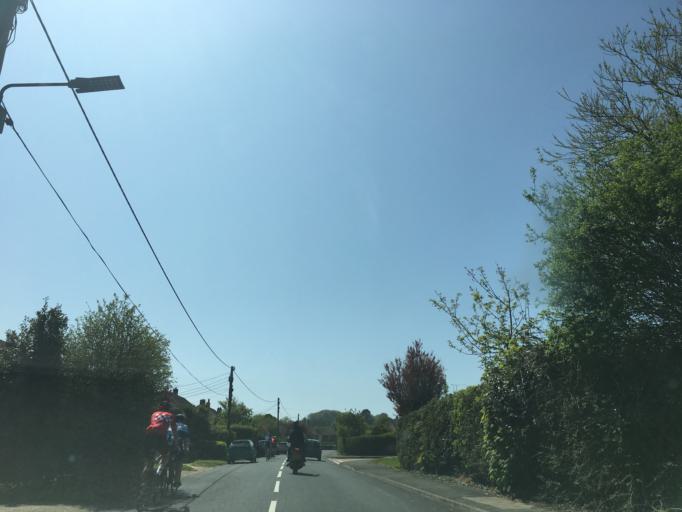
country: GB
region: England
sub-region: Isle of Wight
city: Niton
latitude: 50.5896
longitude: -1.2791
